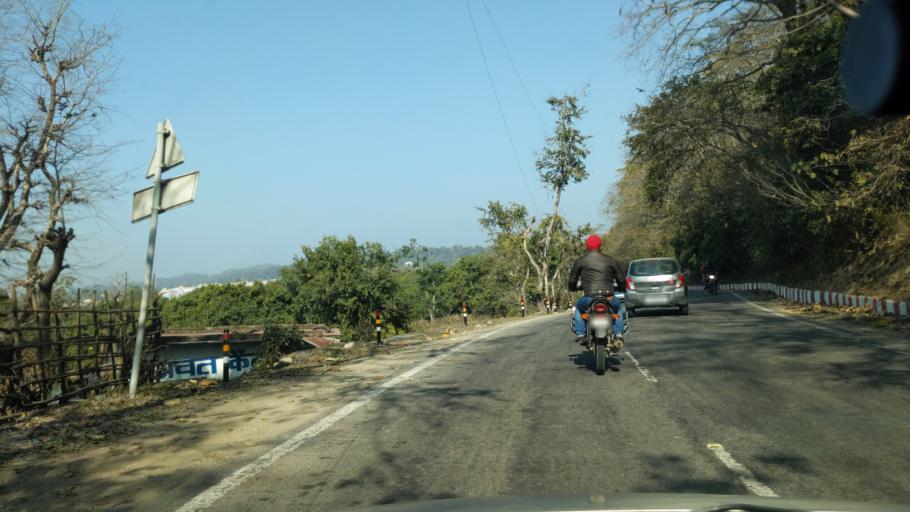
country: IN
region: Uttarakhand
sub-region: Naini Tal
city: Ramnagar
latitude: 29.3863
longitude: 79.1415
